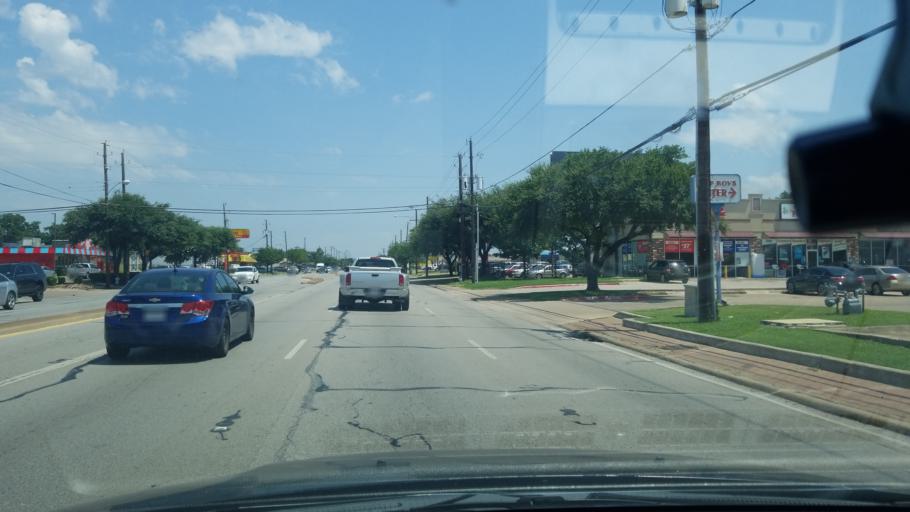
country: US
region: Texas
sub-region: Dallas County
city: Balch Springs
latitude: 32.7422
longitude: -96.6828
